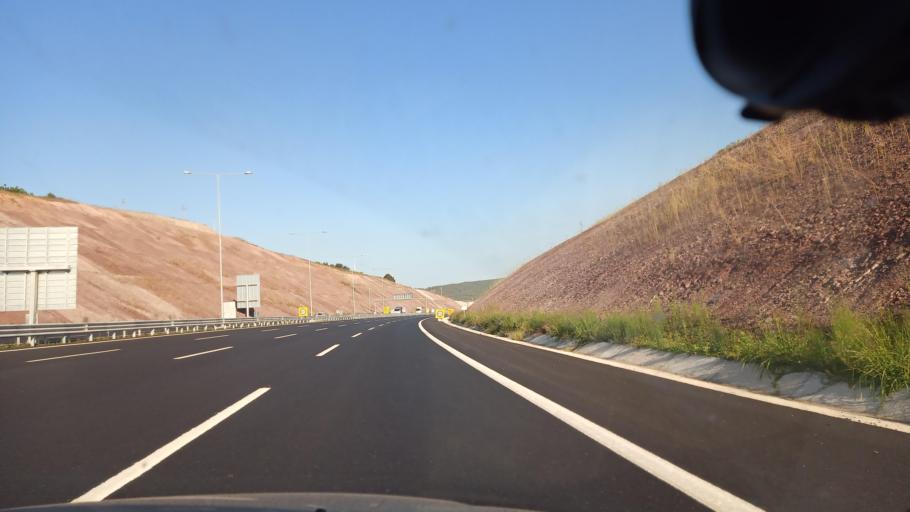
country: TR
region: Sakarya
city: Adapazari
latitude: 40.8392
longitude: 30.3755
